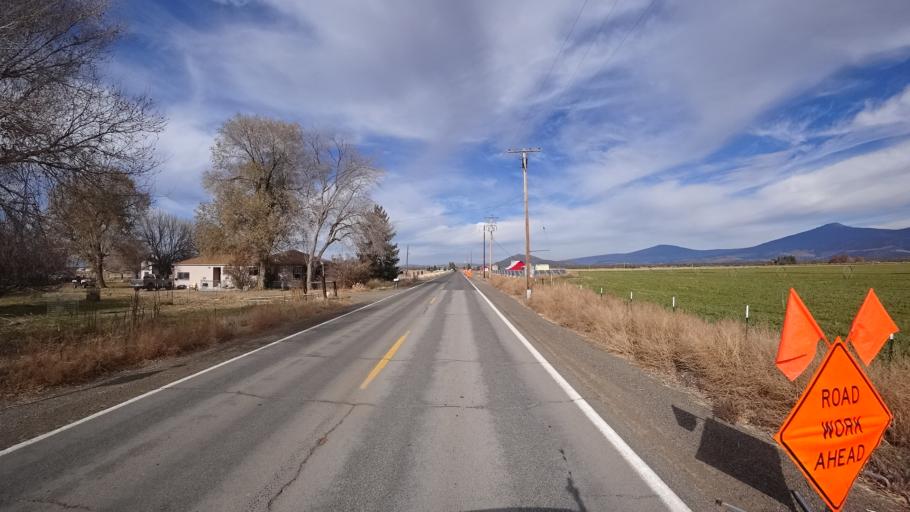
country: US
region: California
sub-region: Siskiyou County
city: Montague
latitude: 41.6184
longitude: -122.3996
